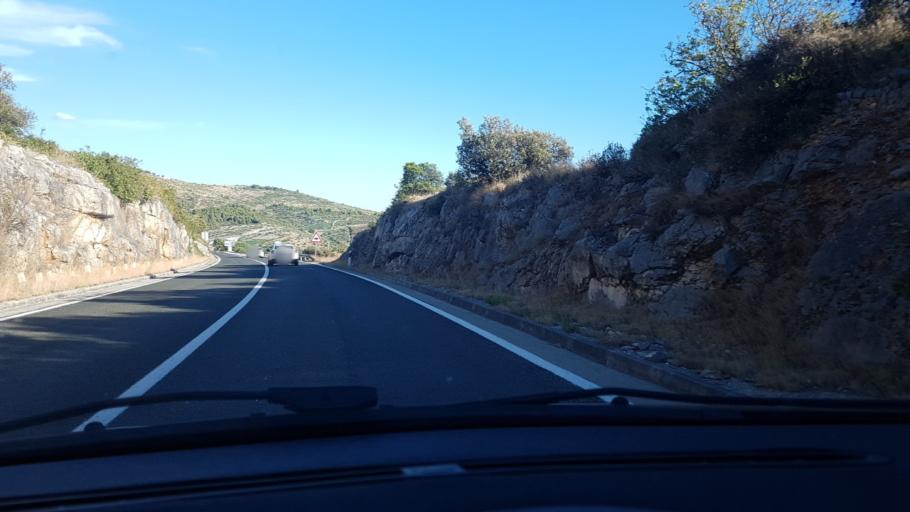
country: HR
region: Sibensko-Kniniska
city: Primosten
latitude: 43.5757
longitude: 15.9394
